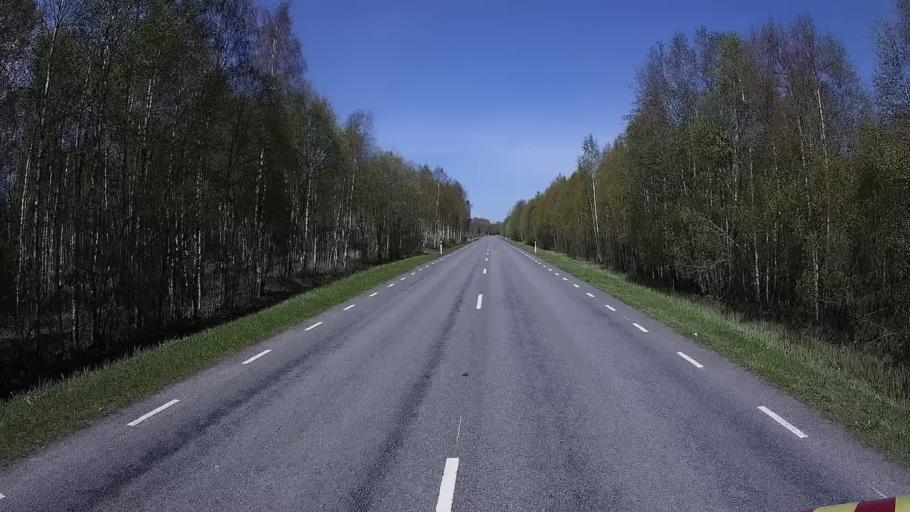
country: EE
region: Laeaene
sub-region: Lihula vald
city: Lihula
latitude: 58.6449
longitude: 23.8491
